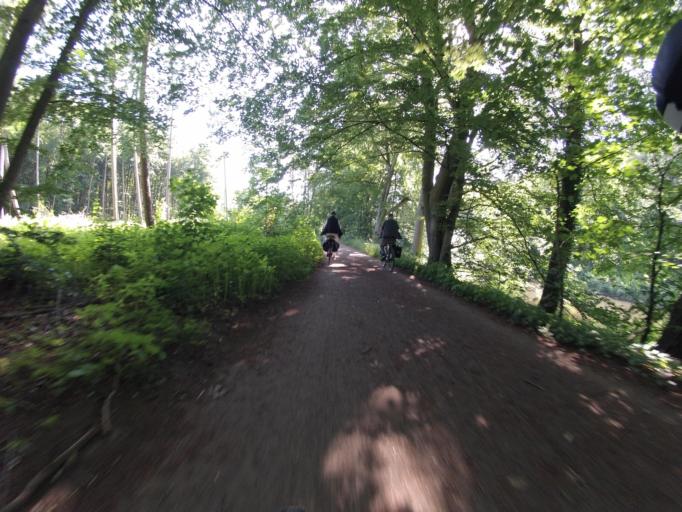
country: DE
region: North Rhine-Westphalia
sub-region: Regierungsbezirk Munster
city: Rheine
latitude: 52.3093
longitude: 7.4139
